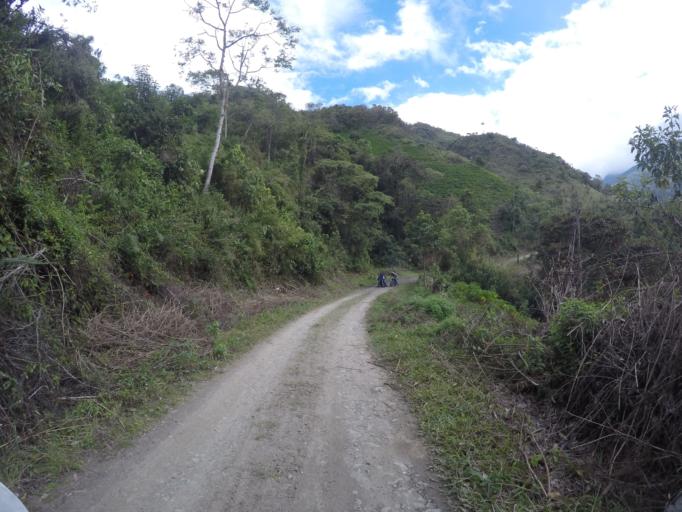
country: CO
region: Tolima
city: Cajamarca
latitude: 4.5311
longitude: -75.4134
